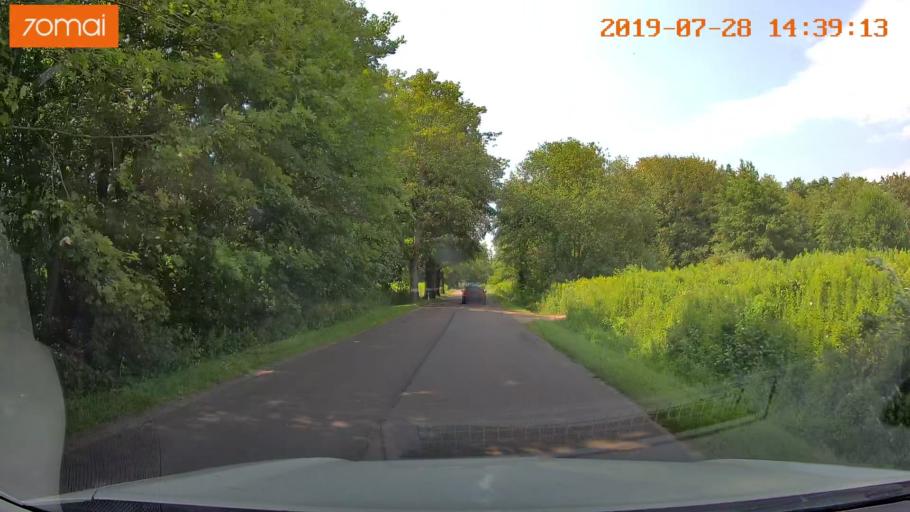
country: RU
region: Kaliningrad
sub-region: Gorod Kaliningrad
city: Yantarnyy
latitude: 54.8469
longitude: 19.9727
